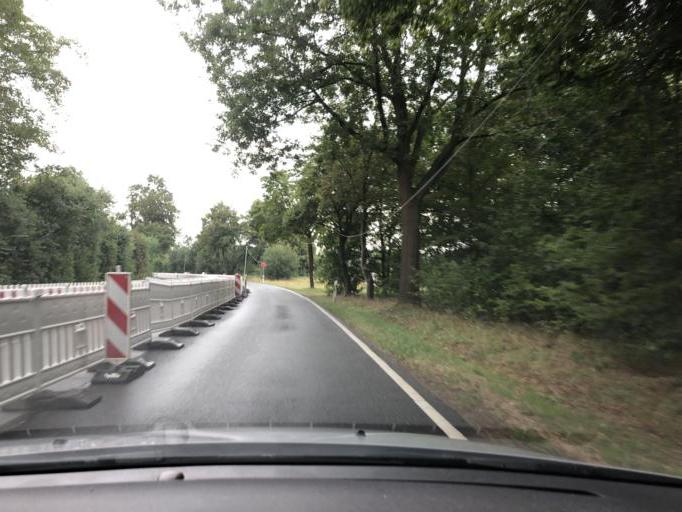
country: DE
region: North Rhine-Westphalia
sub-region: Regierungsbezirk Dusseldorf
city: Schermbeck
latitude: 51.6774
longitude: 6.8609
